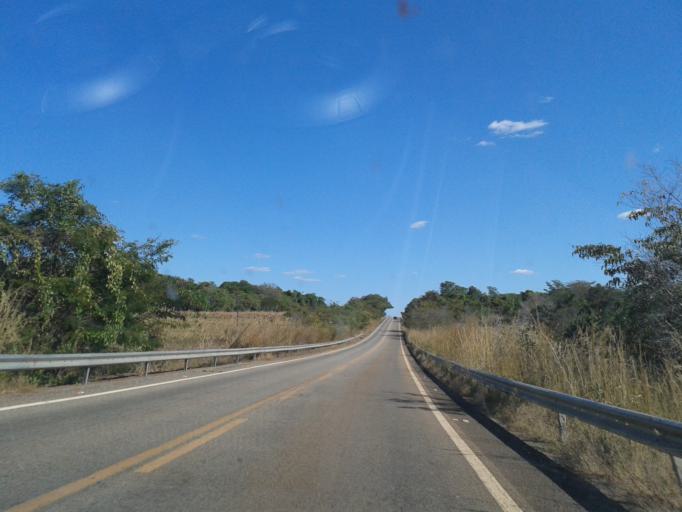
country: BR
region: Goias
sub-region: Mozarlandia
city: Mozarlandia
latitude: -14.3097
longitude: -50.4054
